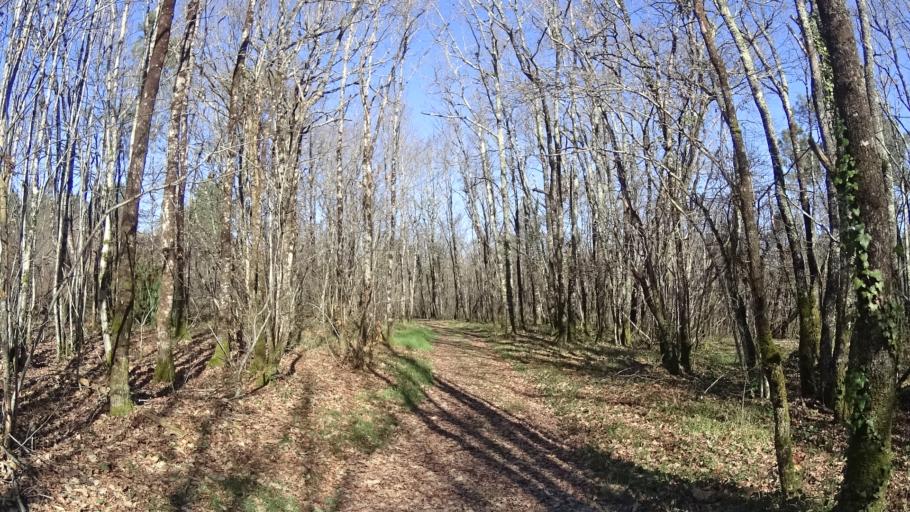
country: FR
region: Aquitaine
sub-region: Departement de la Dordogne
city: Saint-Aulaye
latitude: 45.2249
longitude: 0.1184
